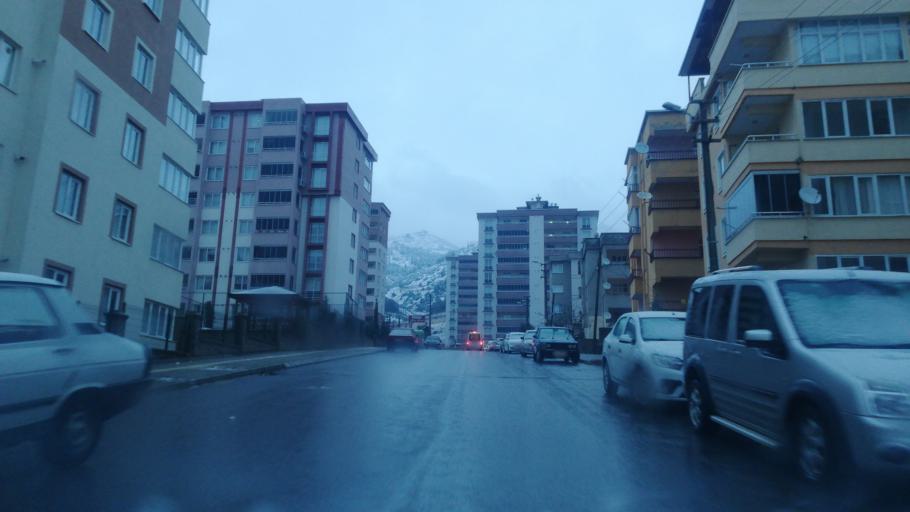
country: TR
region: Kahramanmaras
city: Kahramanmaras
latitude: 37.5994
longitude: 36.8824
